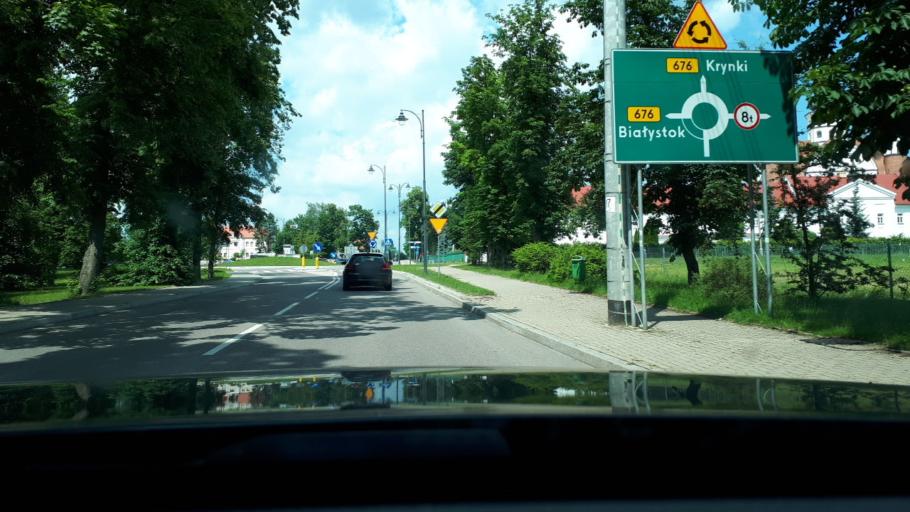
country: PL
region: Podlasie
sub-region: Powiat bialostocki
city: Suprasl
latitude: 53.2093
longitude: 23.3364
